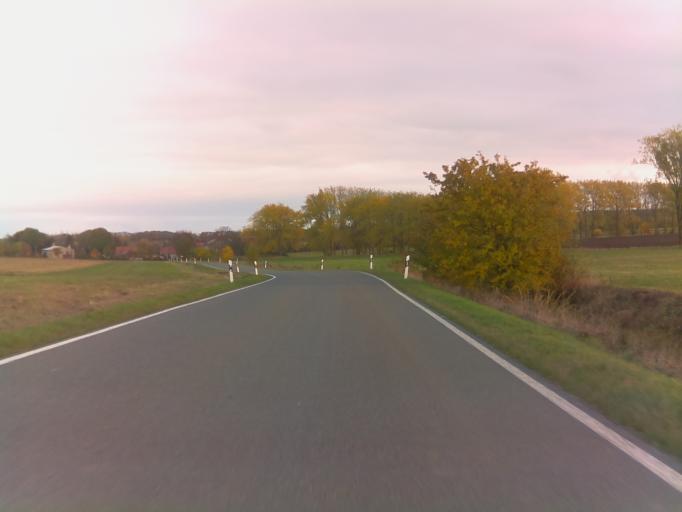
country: DE
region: Thuringia
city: Milda
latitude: 50.8399
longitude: 11.4066
